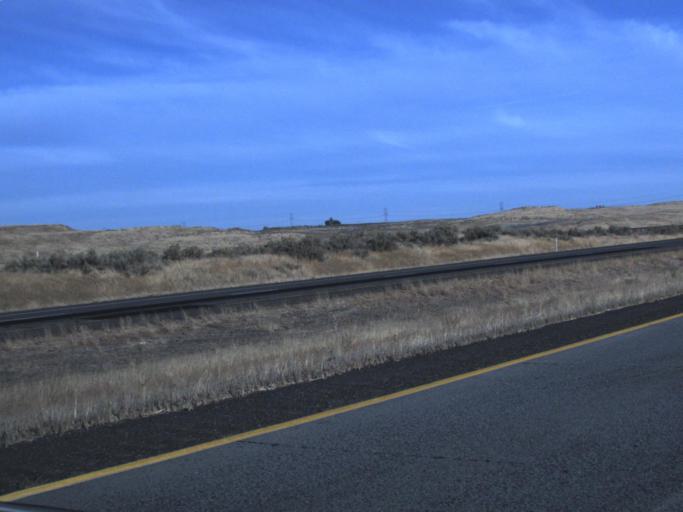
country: US
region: Washington
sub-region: Franklin County
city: Basin City
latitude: 46.5293
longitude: -119.0149
